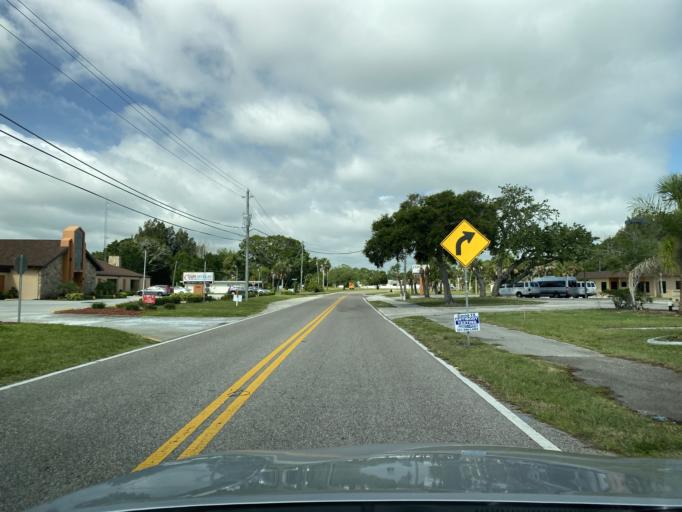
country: US
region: Florida
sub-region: Brevard County
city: Palm Bay
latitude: 28.0351
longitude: -80.5868
